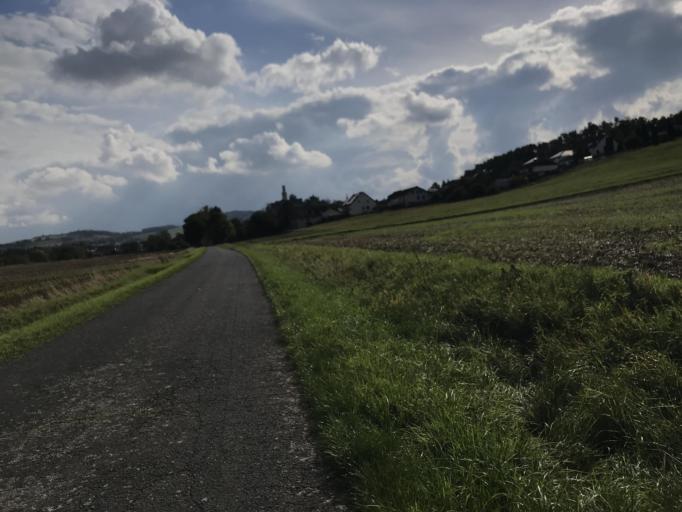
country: DE
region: Hesse
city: Felsberg
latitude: 51.1445
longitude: 9.4193
